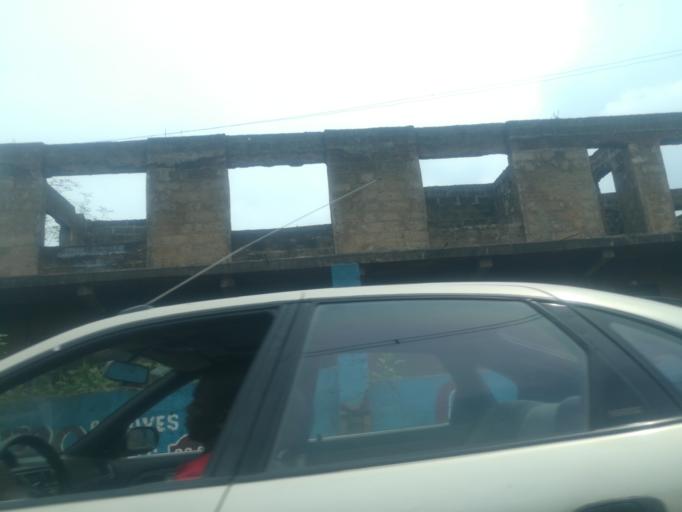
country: NG
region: Oyo
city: Ibadan
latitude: 7.4308
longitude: 3.9211
